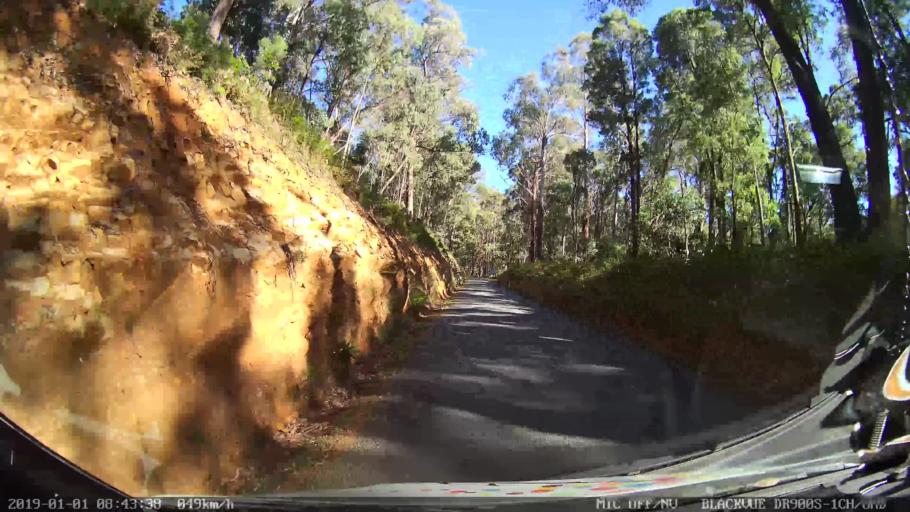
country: AU
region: New South Wales
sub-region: Snowy River
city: Jindabyne
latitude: -36.3159
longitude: 148.1924
